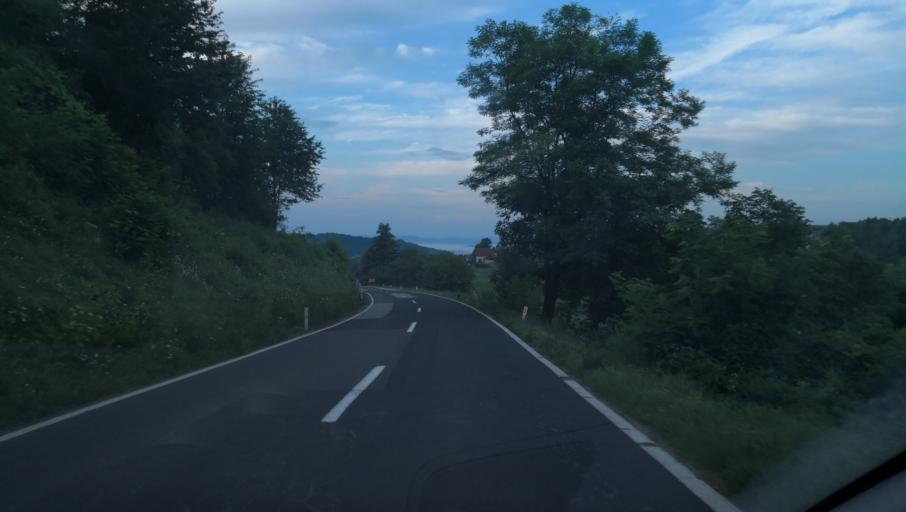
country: SI
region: Metlika
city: Metlika
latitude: 45.6776
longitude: 15.2847
